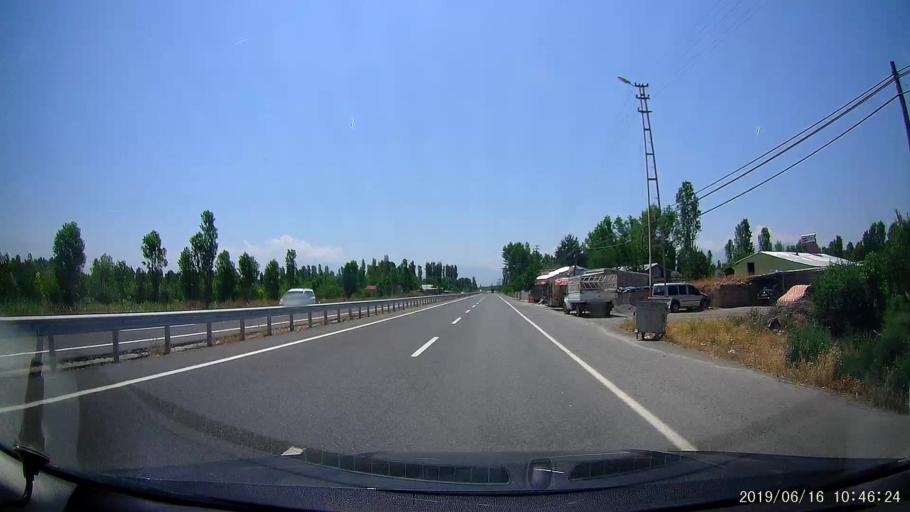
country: AM
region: Armavir
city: Shenavan
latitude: 40.0222
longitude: 43.8790
